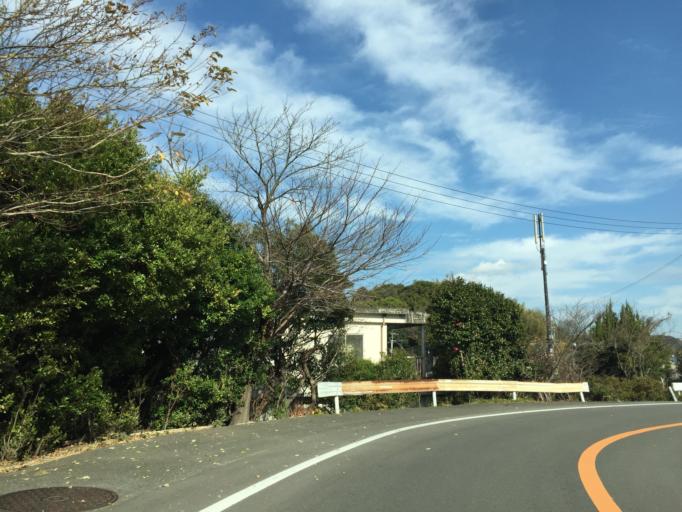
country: JP
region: Wakayama
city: Kainan
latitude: 34.1711
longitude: 135.2245
